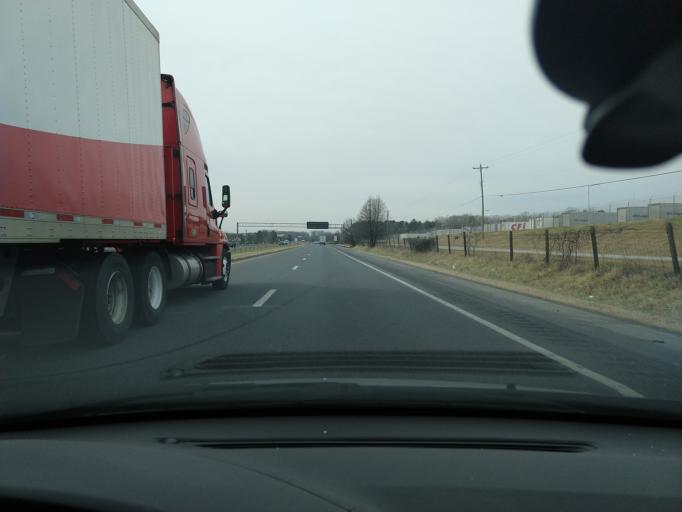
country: US
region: South Carolina
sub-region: Cherokee County
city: East Gaffney
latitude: 35.1027
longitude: -81.6311
